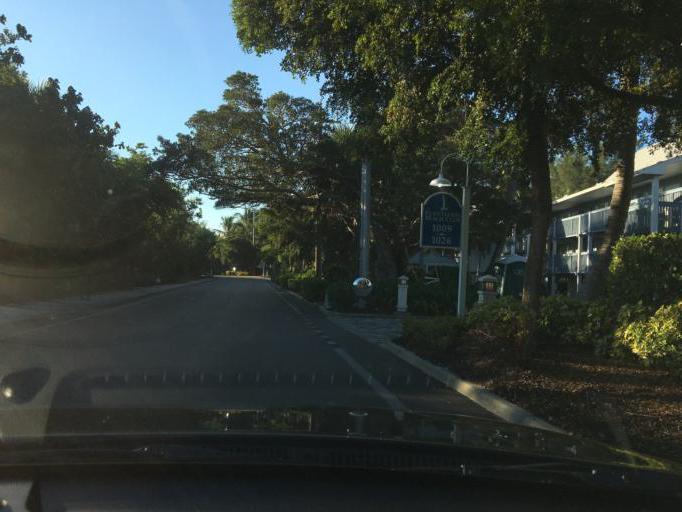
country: US
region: Florida
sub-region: Lee County
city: Pine Island Center
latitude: 26.5427
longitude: -82.1964
